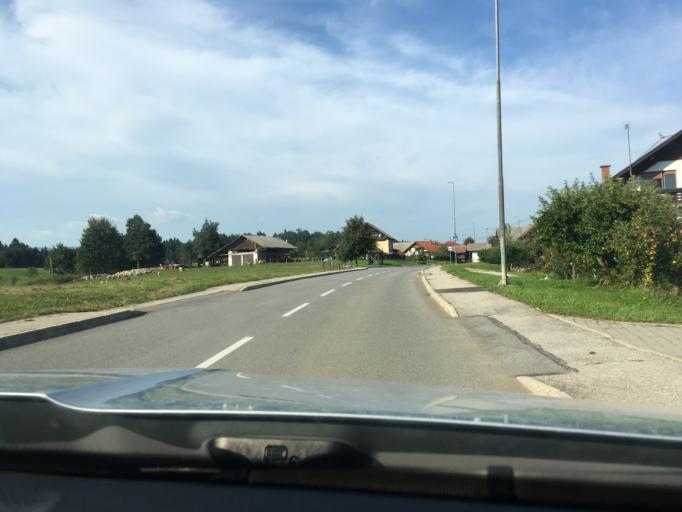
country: SI
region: Crnomelj
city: Crnomelj
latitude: 45.5997
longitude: 15.2310
